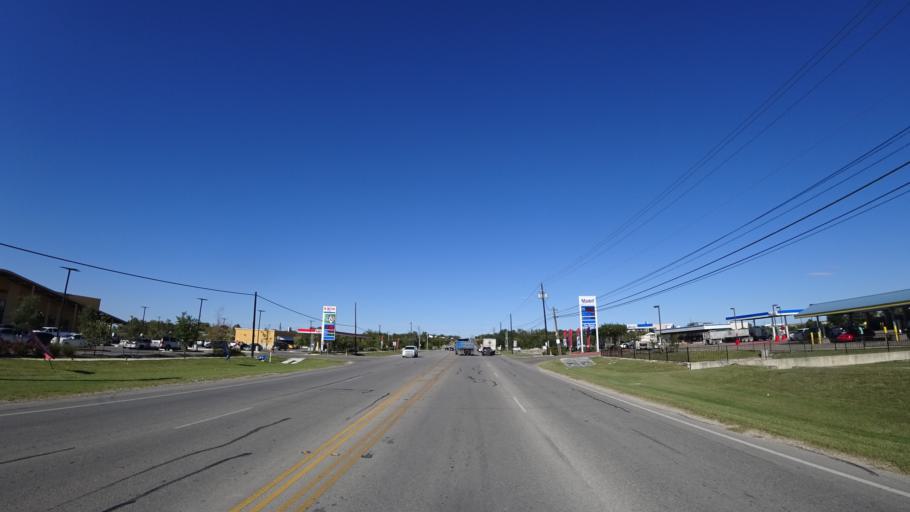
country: US
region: Texas
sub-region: Travis County
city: Hornsby Bend
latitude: 30.2898
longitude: -97.6289
